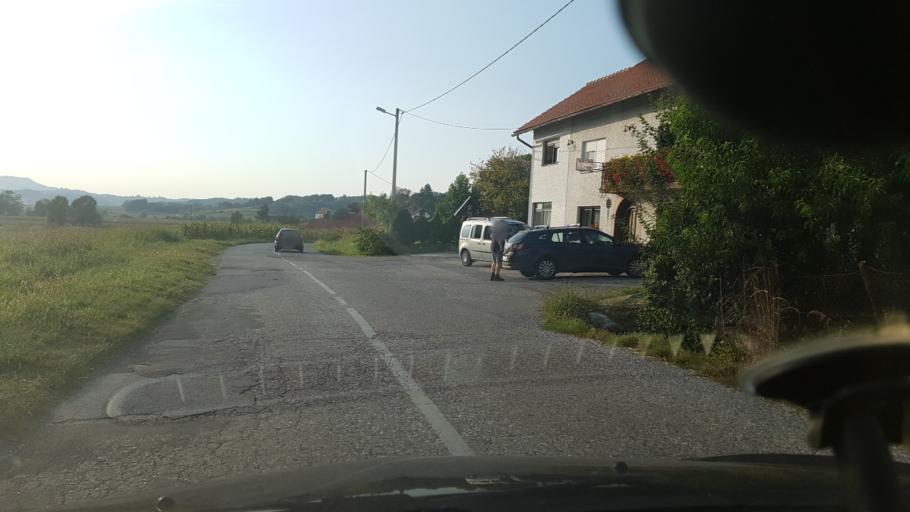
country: HR
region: Krapinsko-Zagorska
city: Zabok
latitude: 46.0314
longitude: 15.8597
